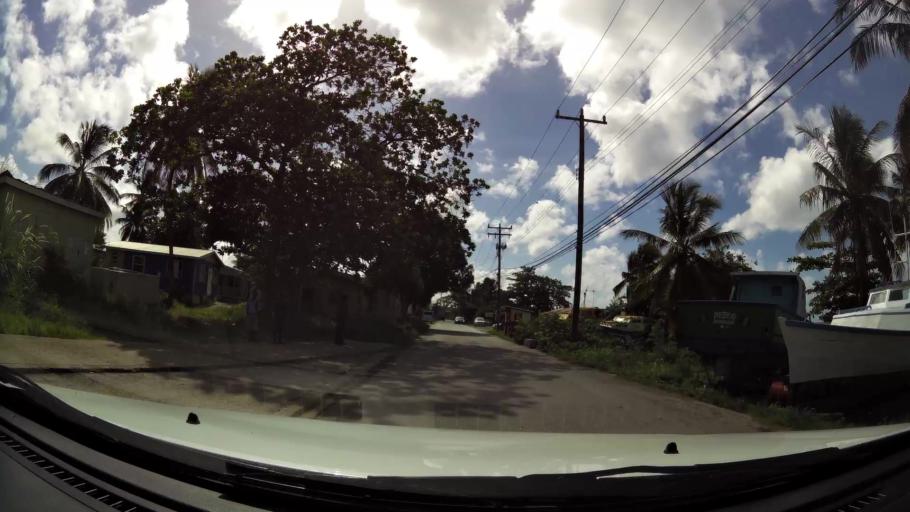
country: BB
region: Saint Lucy
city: Checker Hall
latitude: 13.2686
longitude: -59.6450
